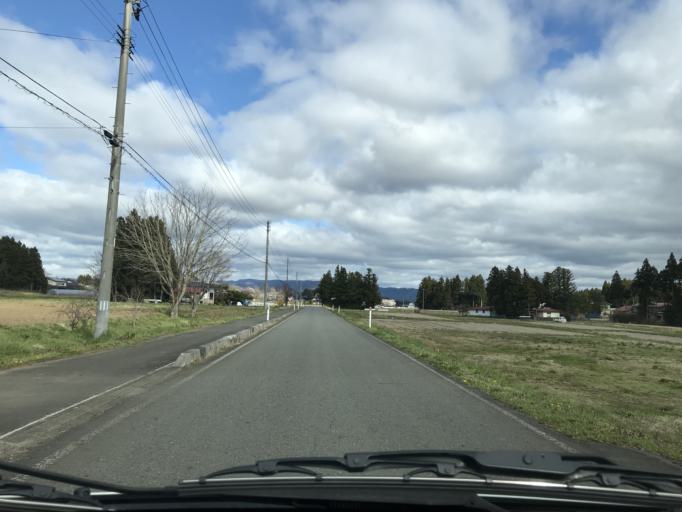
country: JP
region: Iwate
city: Mizusawa
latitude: 39.0961
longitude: 141.0717
